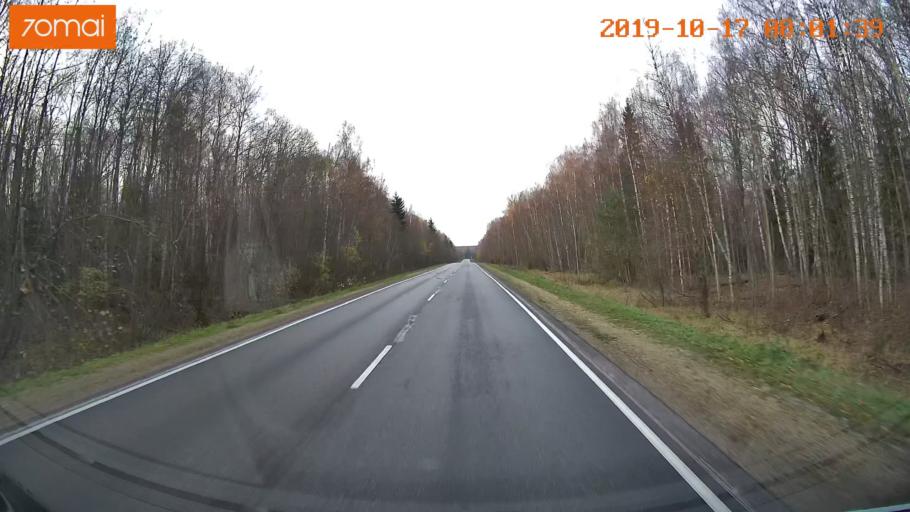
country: RU
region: Vladimir
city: Bavleny
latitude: 56.3707
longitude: 39.4920
